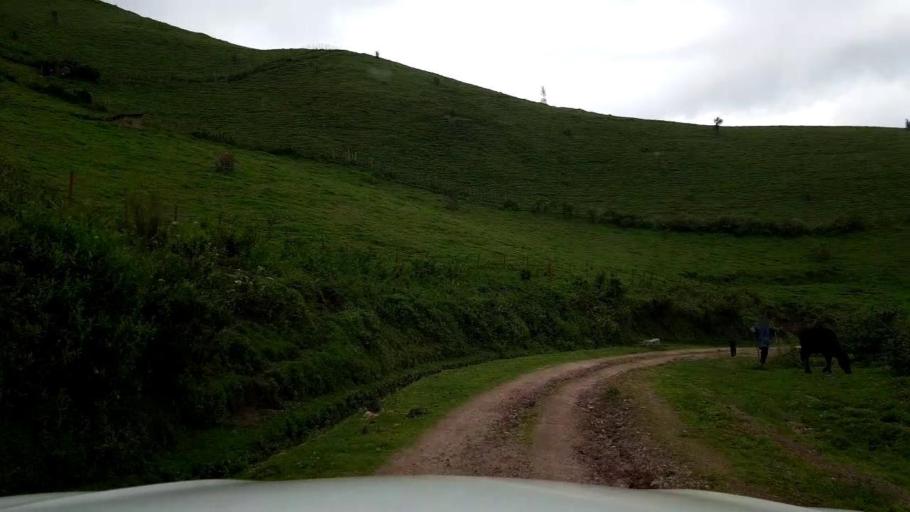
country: RW
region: Western Province
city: Gisenyi
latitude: -1.6792
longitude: 29.4185
